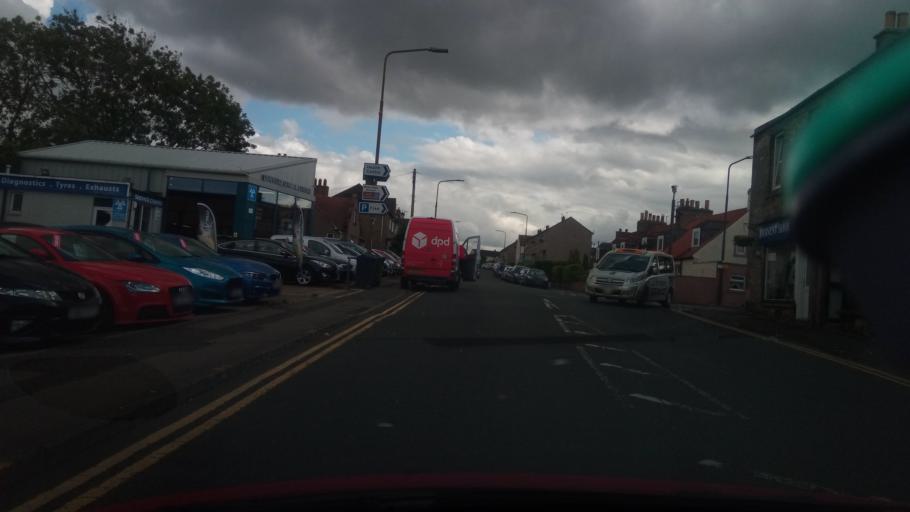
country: GB
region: Scotland
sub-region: East Lothian
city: Tranent
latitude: 55.9431
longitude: -2.9492
